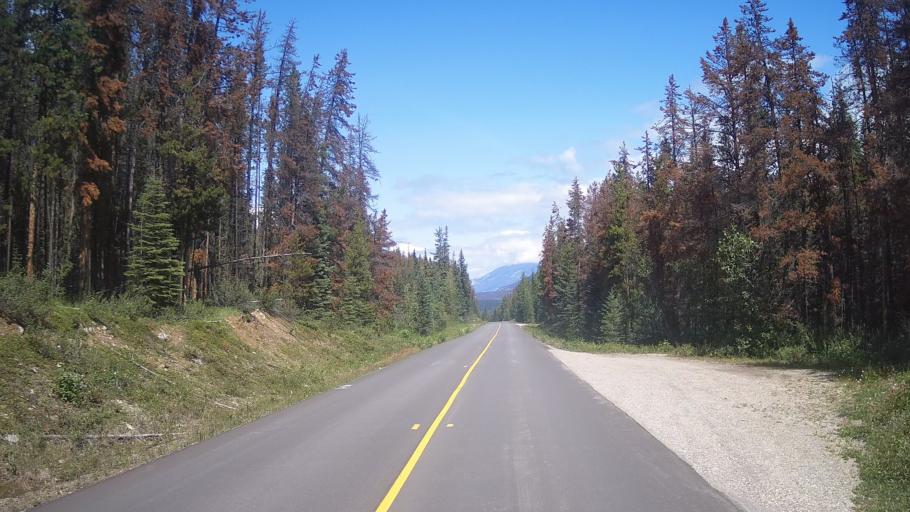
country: CA
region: Alberta
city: Jasper Park Lodge
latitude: 52.7798
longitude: -118.0325
